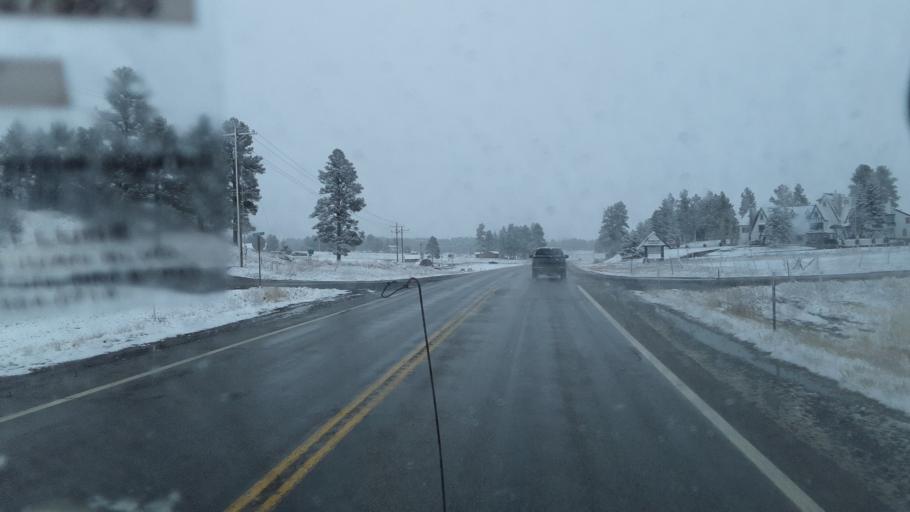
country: US
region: Colorado
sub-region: Archuleta County
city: Pagosa Springs
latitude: 37.2219
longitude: -106.9852
